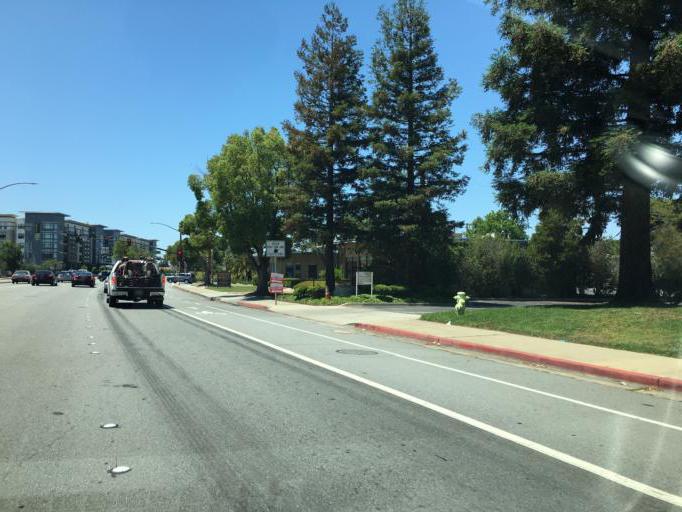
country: US
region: California
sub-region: San Mateo County
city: Redwood City
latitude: 37.4909
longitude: -122.2295
